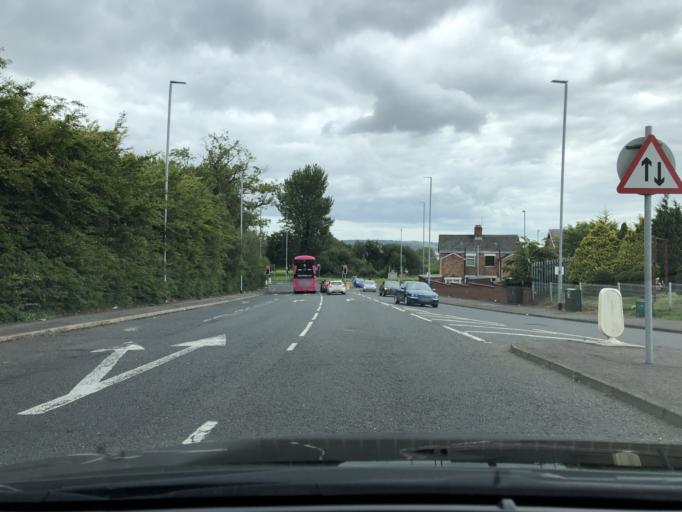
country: GB
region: Northern Ireland
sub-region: Newtownabbey District
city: Newtownabbey
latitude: 54.6551
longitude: -5.9137
